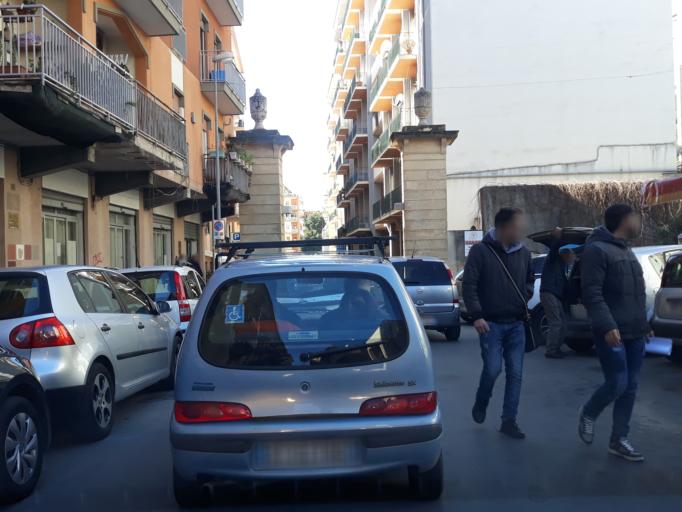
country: IT
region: Sicily
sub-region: Palermo
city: Monreale
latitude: 38.0791
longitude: 13.2853
